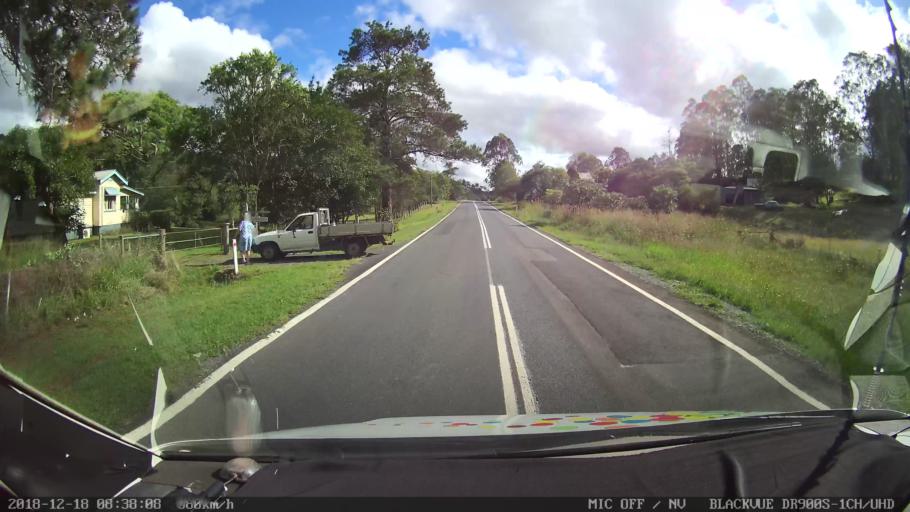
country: AU
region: New South Wales
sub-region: Kyogle
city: Kyogle
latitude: -28.2585
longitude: 152.8247
